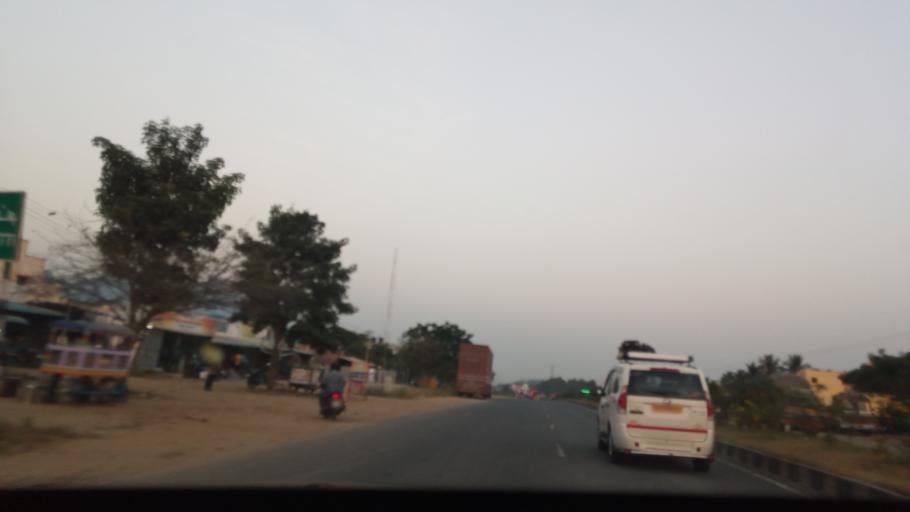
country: IN
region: Tamil Nadu
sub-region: Salem
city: Belur
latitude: 11.6647
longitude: 78.3052
